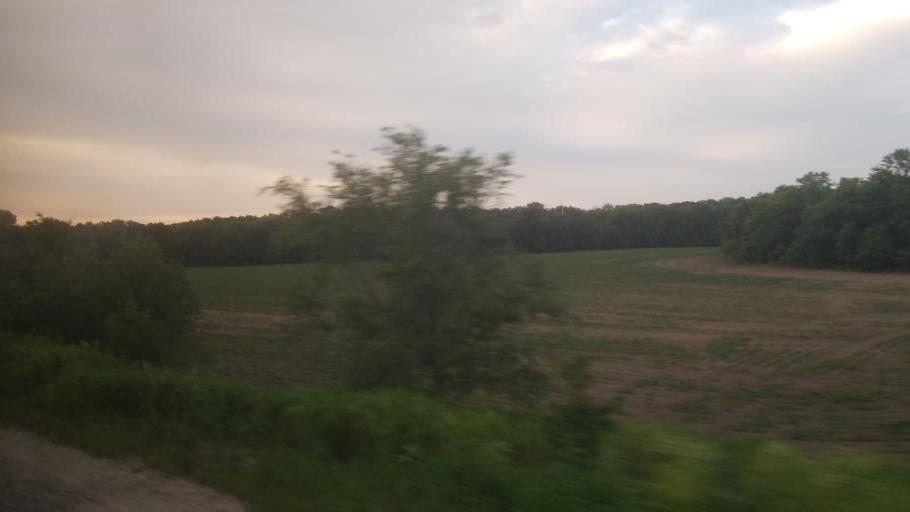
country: US
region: Kansas
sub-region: Marion County
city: Peabody
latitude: 38.1654
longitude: -97.0969
